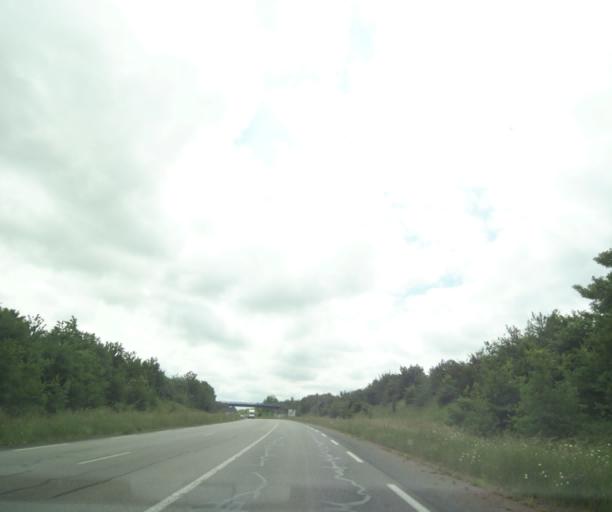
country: FR
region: Poitou-Charentes
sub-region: Departement des Deux-Sevres
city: Le Tallud
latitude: 46.6344
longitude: -0.2762
